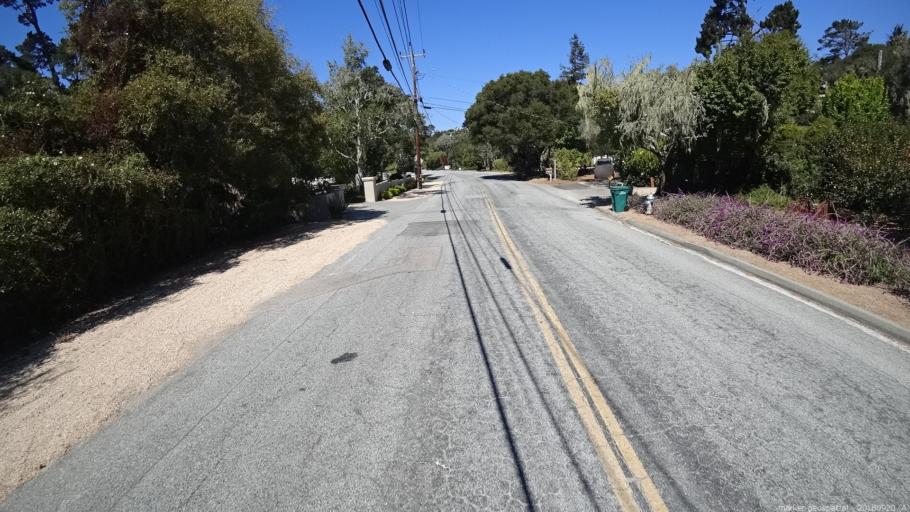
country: US
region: California
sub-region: Monterey County
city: Seaside
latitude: 36.5844
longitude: -121.8666
